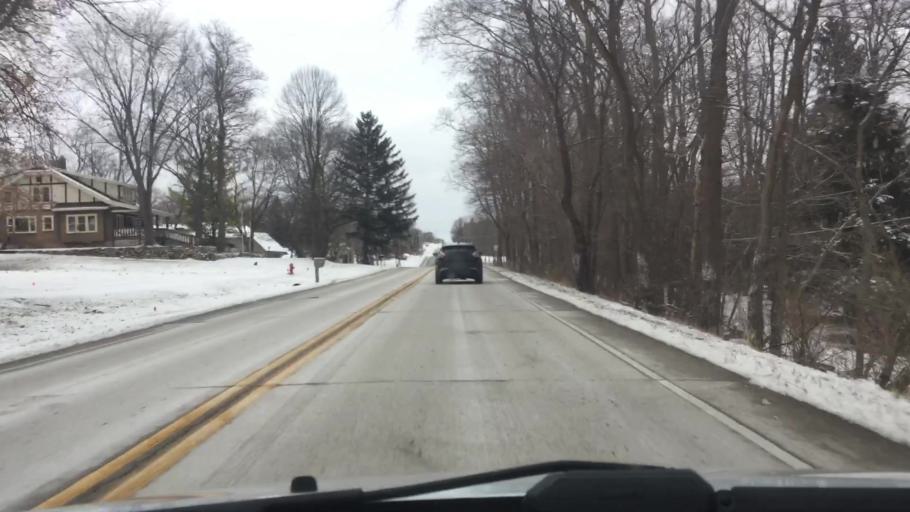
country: US
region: Wisconsin
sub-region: Waukesha County
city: Brookfield
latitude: 43.0713
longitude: -88.1060
